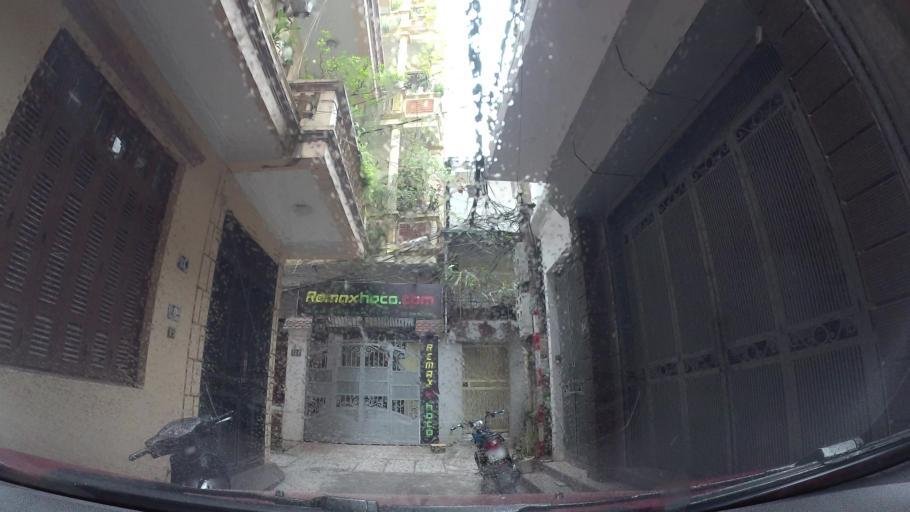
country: VN
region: Ha Noi
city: Dong Da
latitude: 21.0108
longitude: 105.8145
